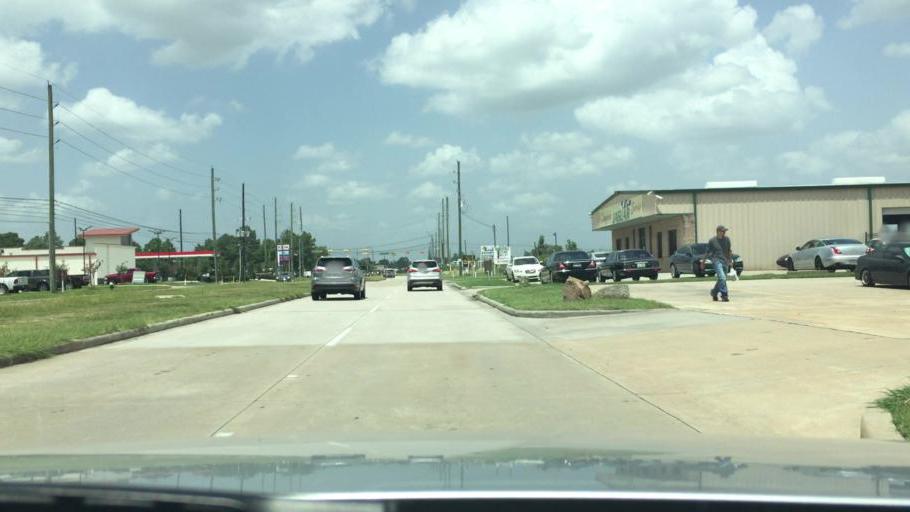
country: US
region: Texas
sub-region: Harris County
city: Hudson
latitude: 29.9546
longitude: -95.5235
